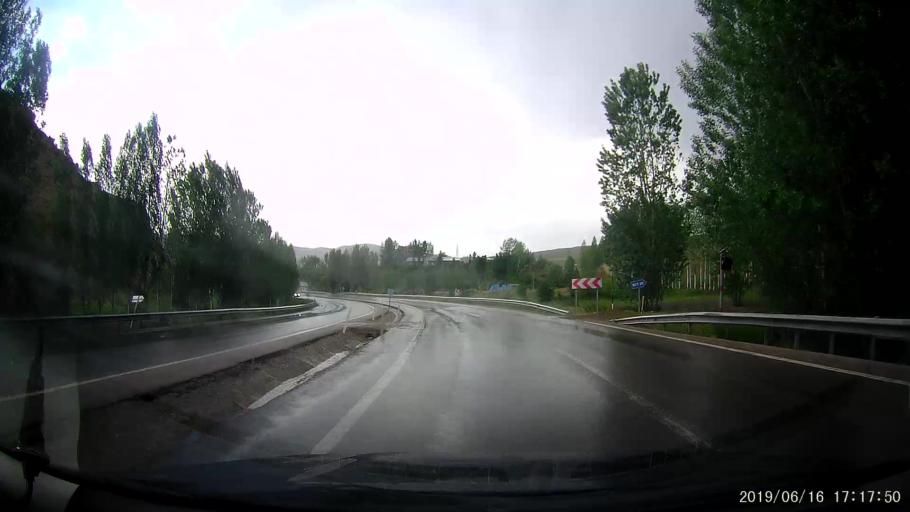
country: TR
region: Erzincan
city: Tercan
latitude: 39.8215
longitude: 40.5306
